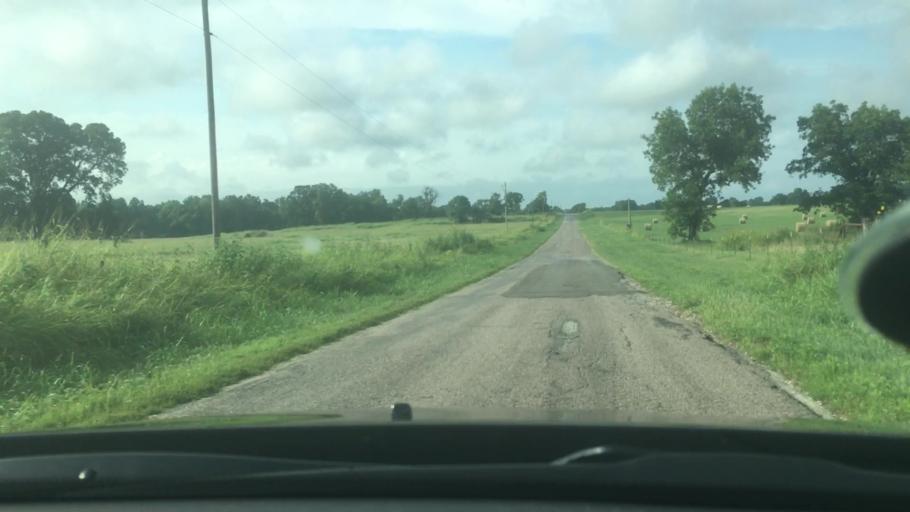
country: US
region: Oklahoma
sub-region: Pontotoc County
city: Ada
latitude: 34.6876
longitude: -96.5298
